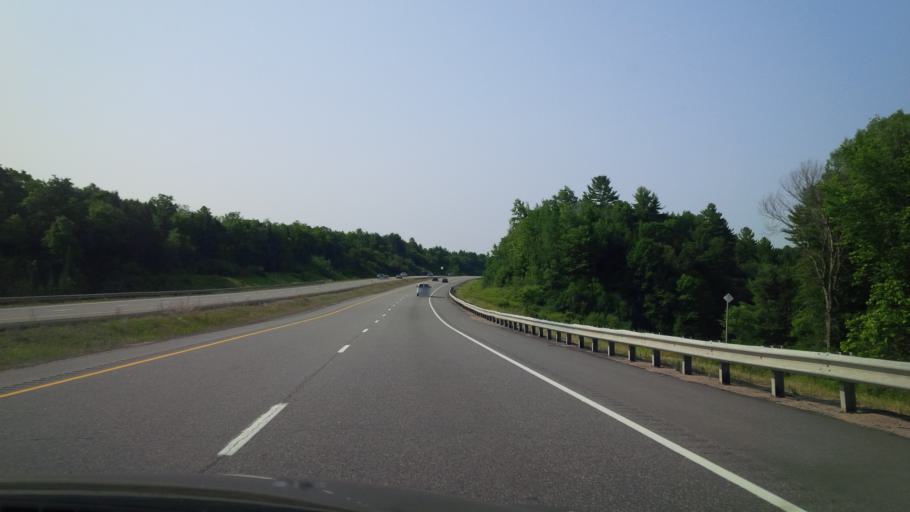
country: CA
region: Ontario
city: Bracebridge
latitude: 45.0289
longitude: -79.2925
